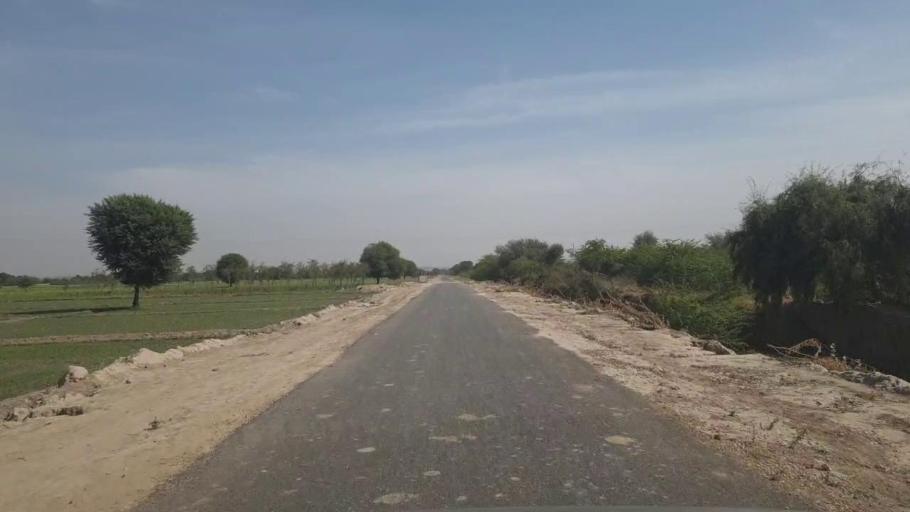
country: PK
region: Sindh
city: Kunri
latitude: 25.1889
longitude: 69.6783
